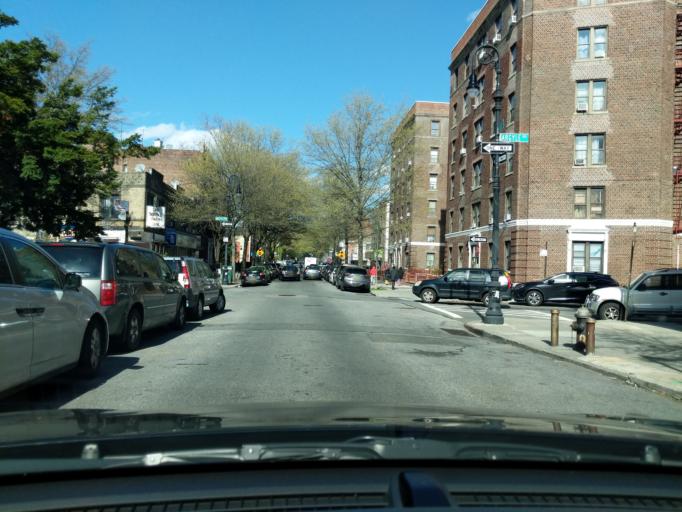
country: US
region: New York
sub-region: Kings County
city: Brooklyn
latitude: 40.6346
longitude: -73.9654
